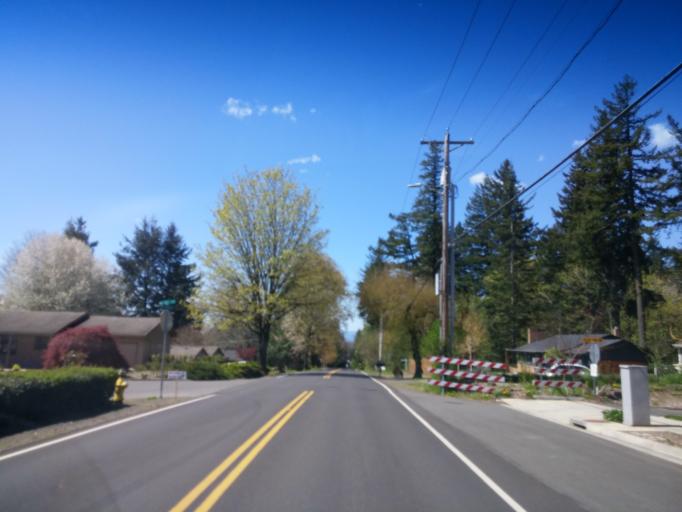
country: US
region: Oregon
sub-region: Washington County
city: West Haven
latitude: 45.5232
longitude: -122.7750
